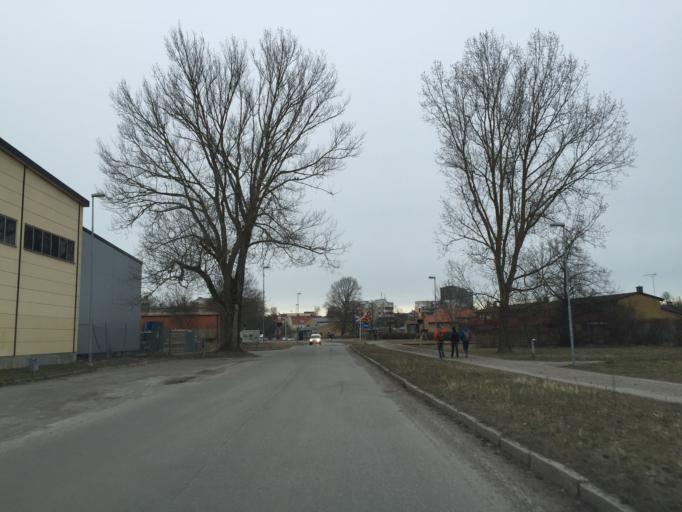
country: SE
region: OErebro
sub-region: Orebro Kommun
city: Orebro
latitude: 59.2619
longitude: 15.2097
